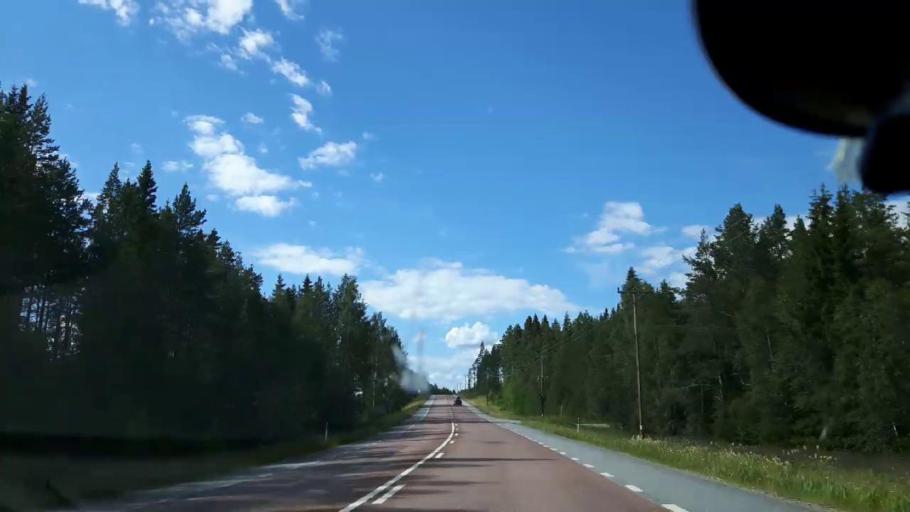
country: SE
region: Jaemtland
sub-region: Braecke Kommun
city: Braecke
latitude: 62.7735
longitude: 15.3987
